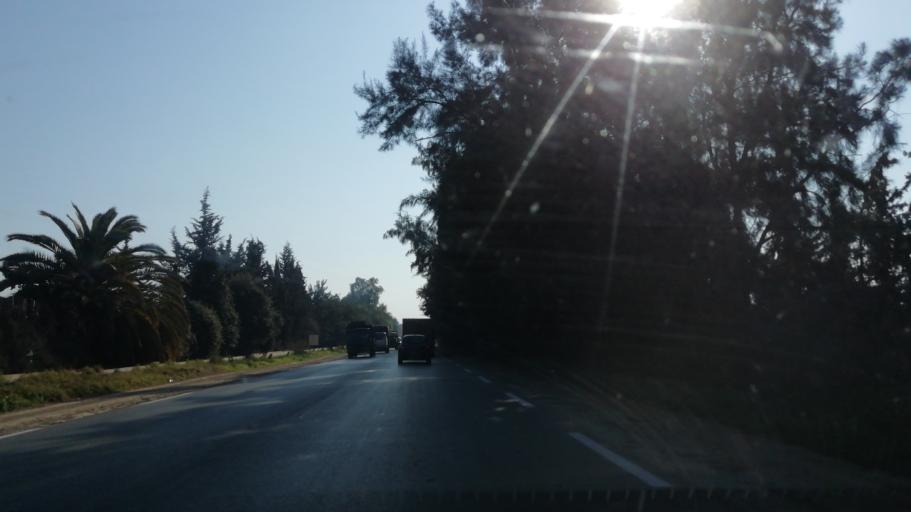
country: DZ
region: Relizane
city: Relizane
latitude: 35.7288
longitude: 0.4757
